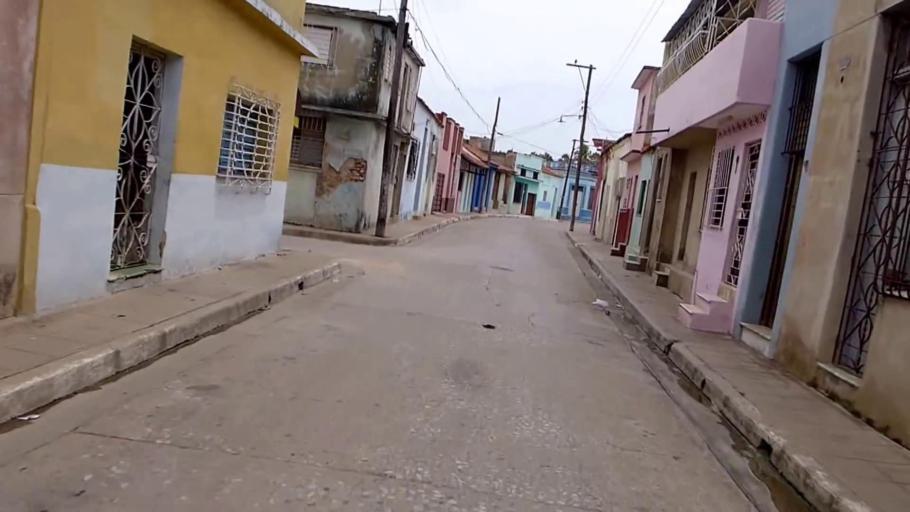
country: CU
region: Camaguey
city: Camaguey
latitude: 21.3785
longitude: -77.9211
